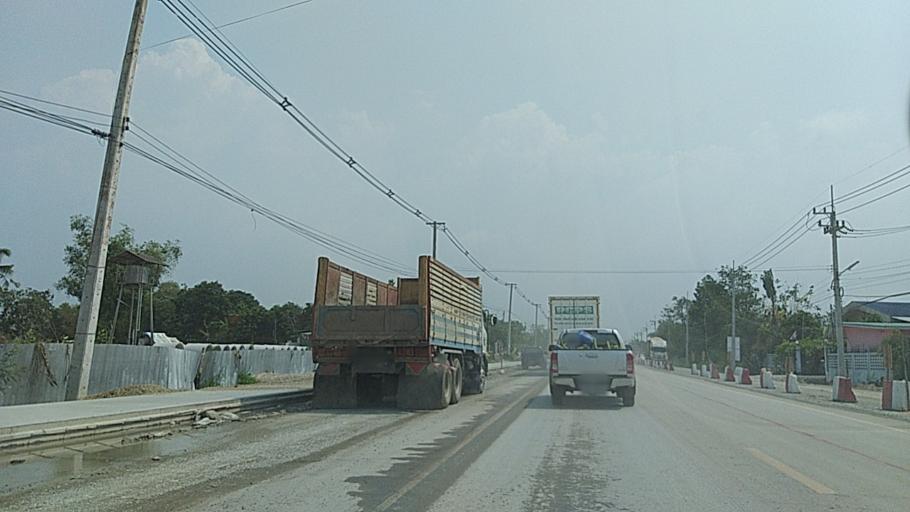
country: TH
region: Chon Buri
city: Phanat Nikhom
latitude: 13.4130
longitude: 101.1886
